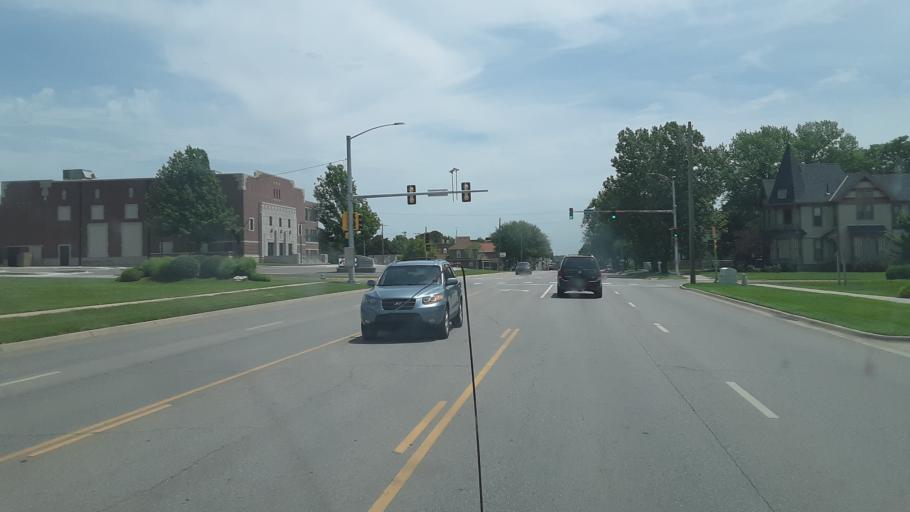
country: US
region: Kansas
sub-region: Butler County
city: El Dorado
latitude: 37.8174
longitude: -96.8575
